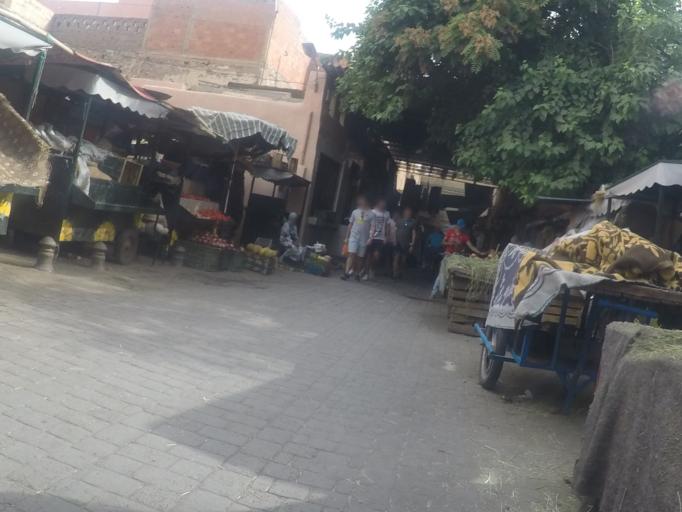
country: MA
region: Marrakech-Tensift-Al Haouz
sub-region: Marrakech
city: Marrakesh
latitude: 31.6303
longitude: -7.9860
